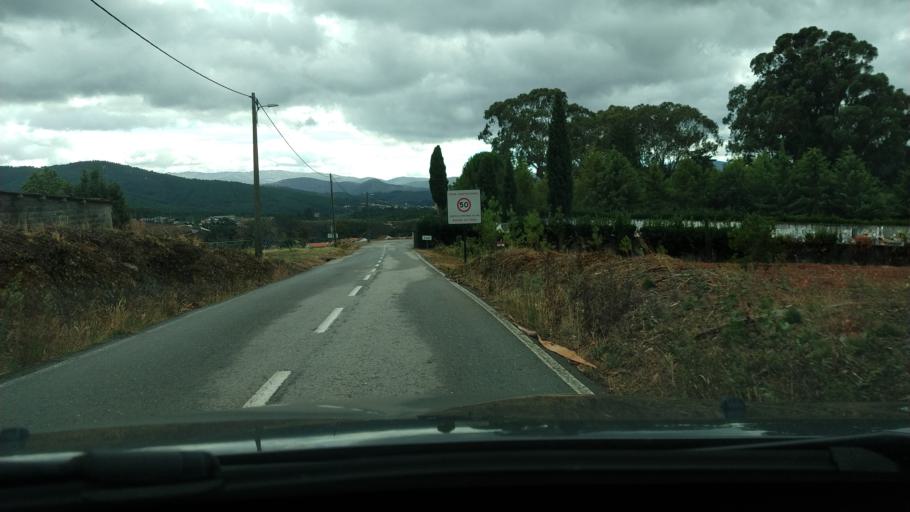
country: PT
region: Castelo Branco
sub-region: Covilha
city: Covilha
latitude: 40.2296
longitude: -7.6479
